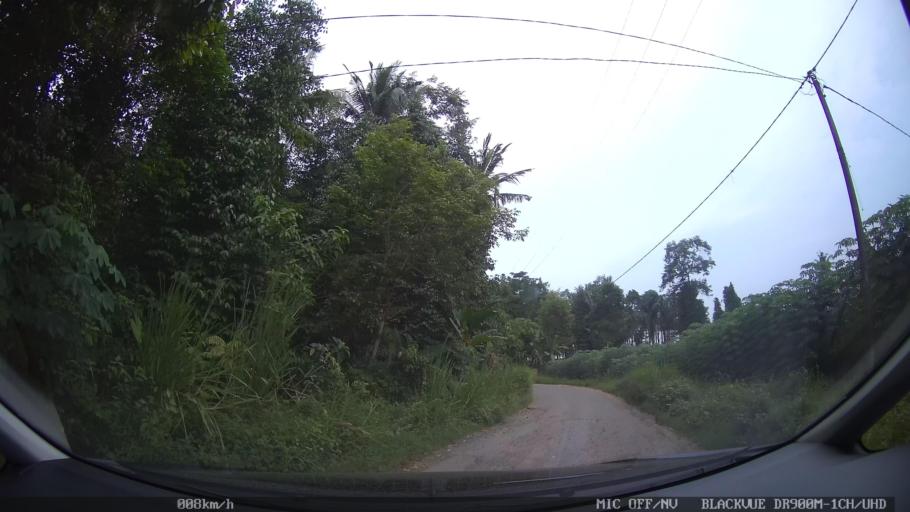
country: ID
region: Lampung
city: Panjang
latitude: -5.4146
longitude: 105.3577
